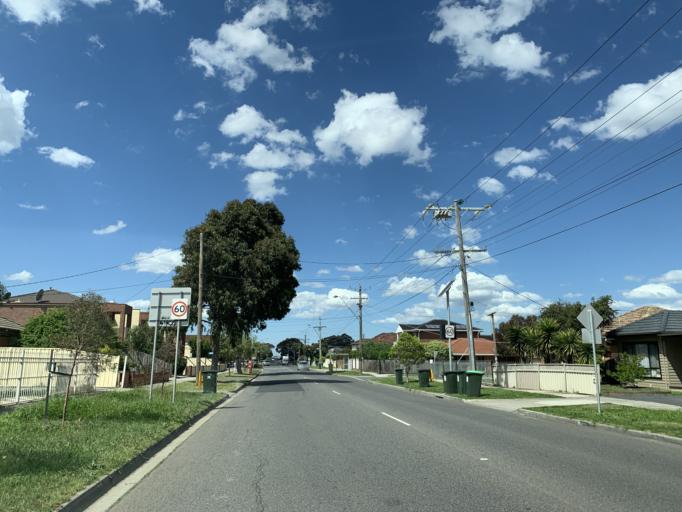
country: AU
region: Victoria
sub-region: Brimbank
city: Albion
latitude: -37.7622
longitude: 144.8272
